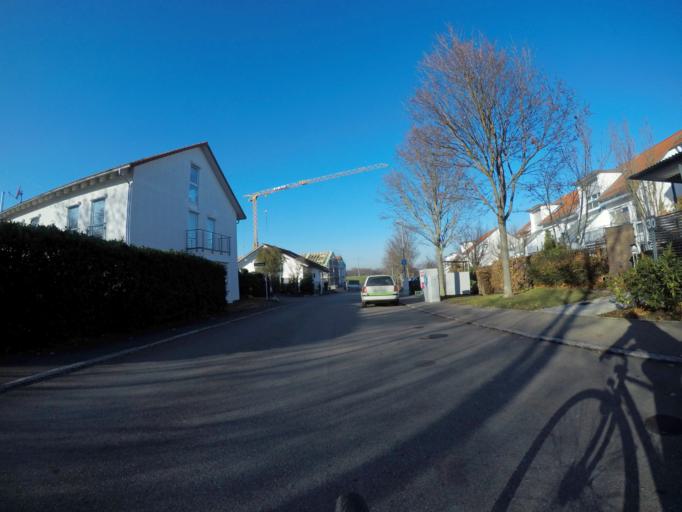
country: DE
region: Baden-Wuerttemberg
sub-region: Tuebingen Region
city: Reutlingen
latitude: 48.5203
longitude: 9.2211
